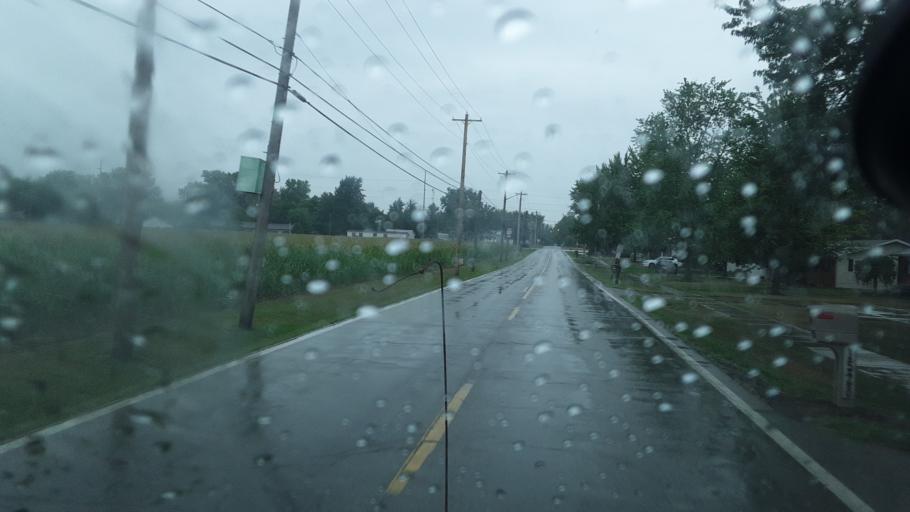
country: US
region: Ohio
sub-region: Williams County
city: Montpelier
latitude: 41.5699
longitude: -84.6131
